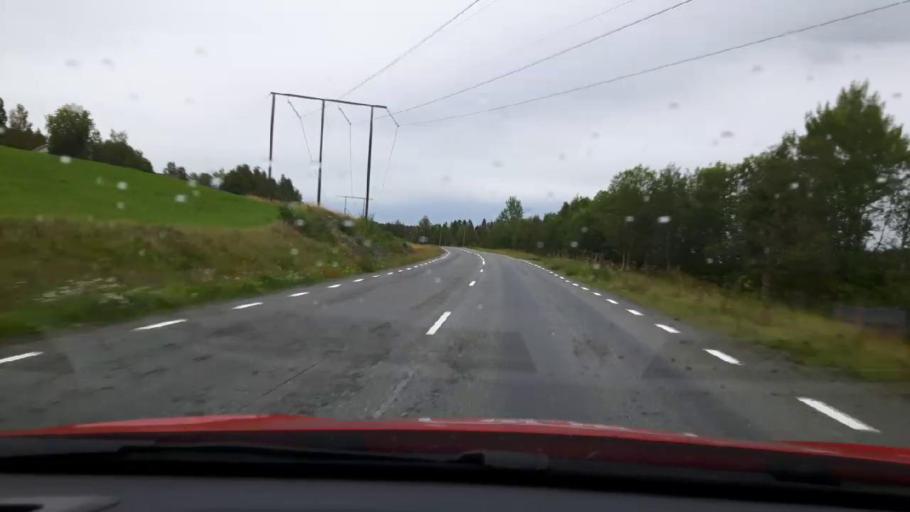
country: SE
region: Jaemtland
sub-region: Are Kommun
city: Jarpen
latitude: 63.3882
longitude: 13.4018
